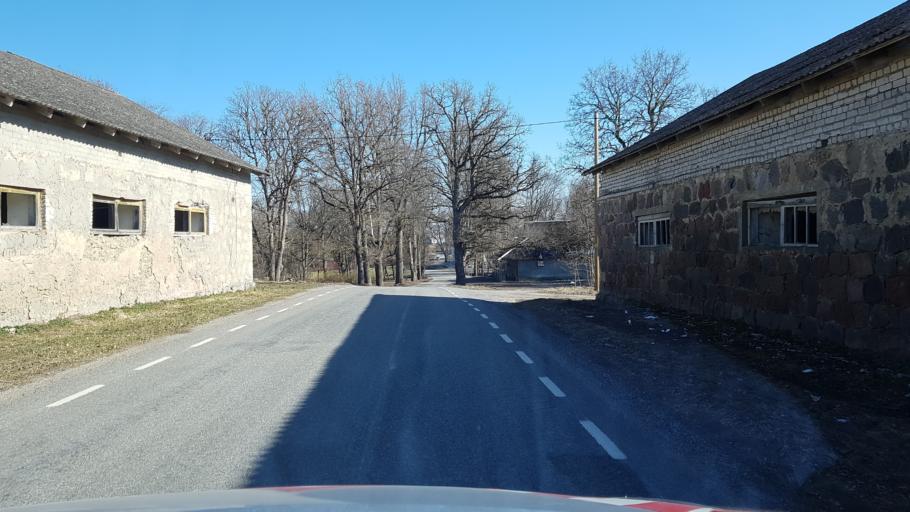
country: EE
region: Laeaene-Virumaa
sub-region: Kadrina vald
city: Kadrina
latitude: 59.3757
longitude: 26.0395
